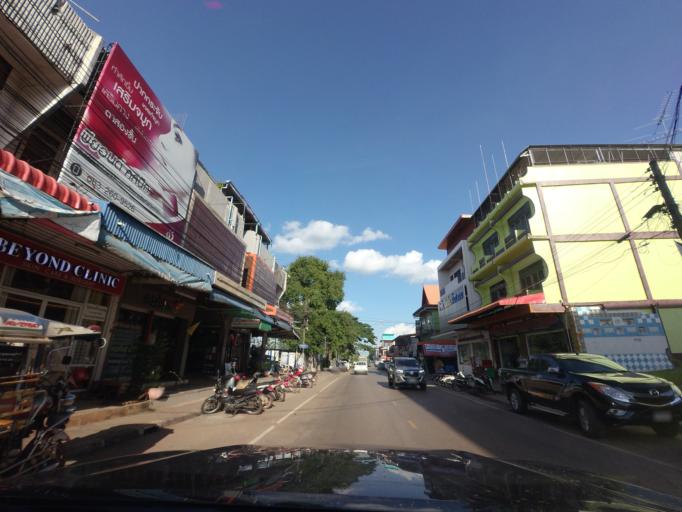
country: TH
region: Changwat Udon Thani
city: Ban Dung
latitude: 17.6982
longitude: 103.2581
